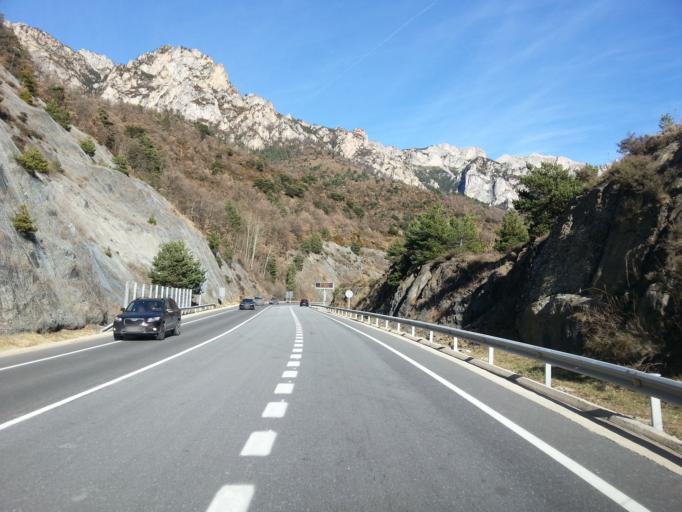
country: ES
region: Catalonia
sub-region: Provincia de Barcelona
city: Baga
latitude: 42.2912
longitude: 1.8584
